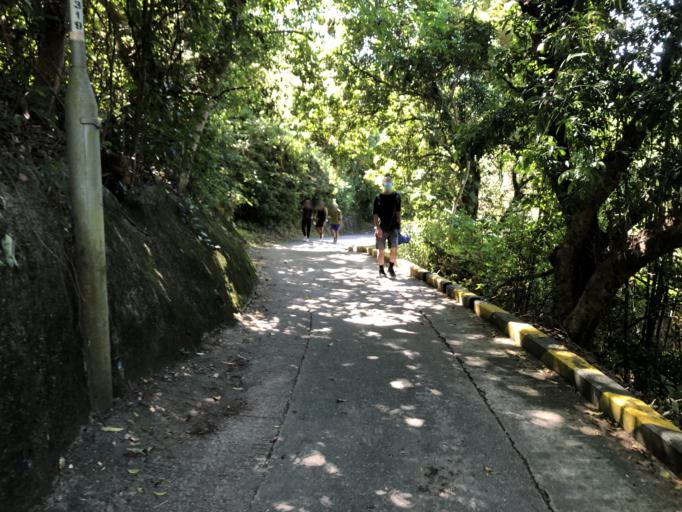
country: HK
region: Tuen Mun
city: Tuen Mun
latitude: 22.2948
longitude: 113.9727
